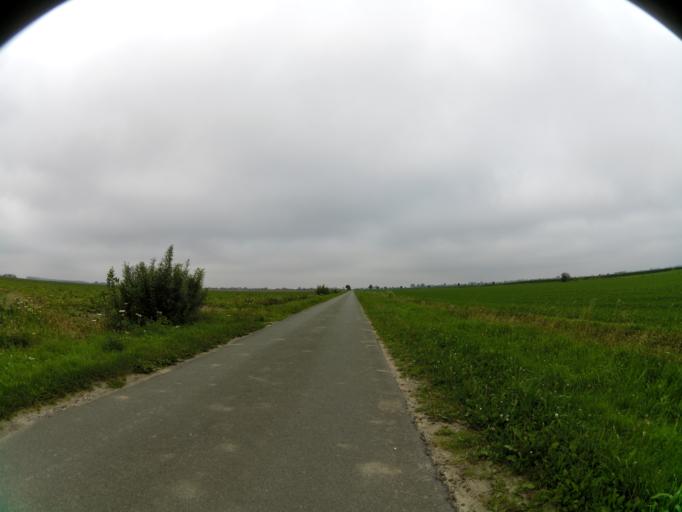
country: BE
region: Flanders
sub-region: Provincie West-Vlaanderen
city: Gistel
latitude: 51.1262
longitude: 2.9513
